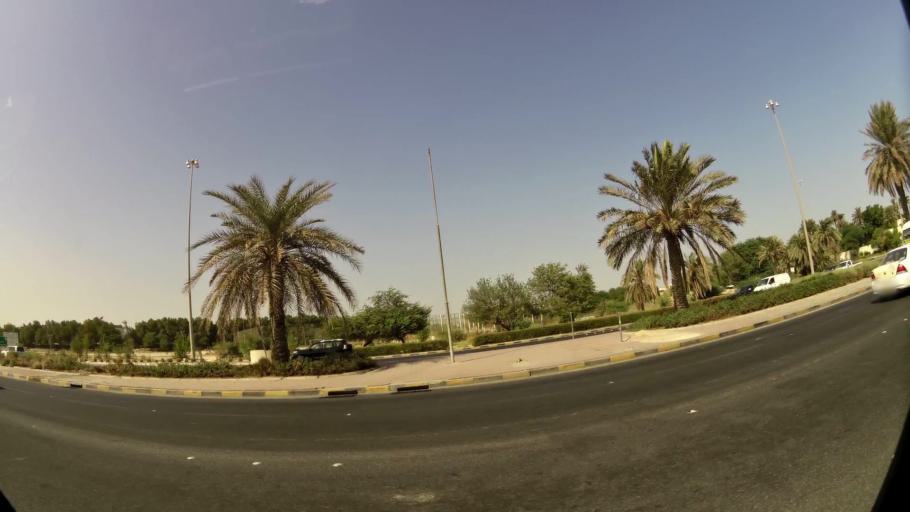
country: KW
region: Muhafazat Hawalli
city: Salwa
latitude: 29.2681
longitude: 48.0832
